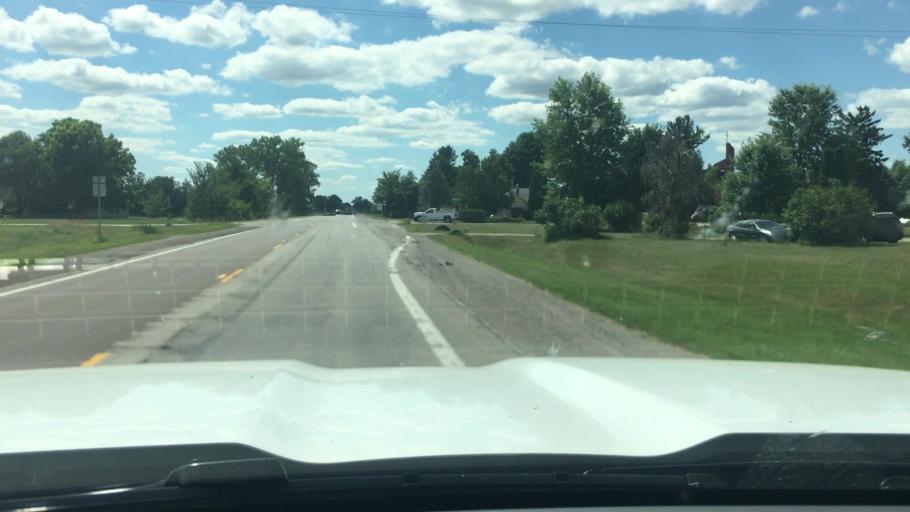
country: US
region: Michigan
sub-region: Saginaw County
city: Chesaning
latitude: 43.1869
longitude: -84.2266
